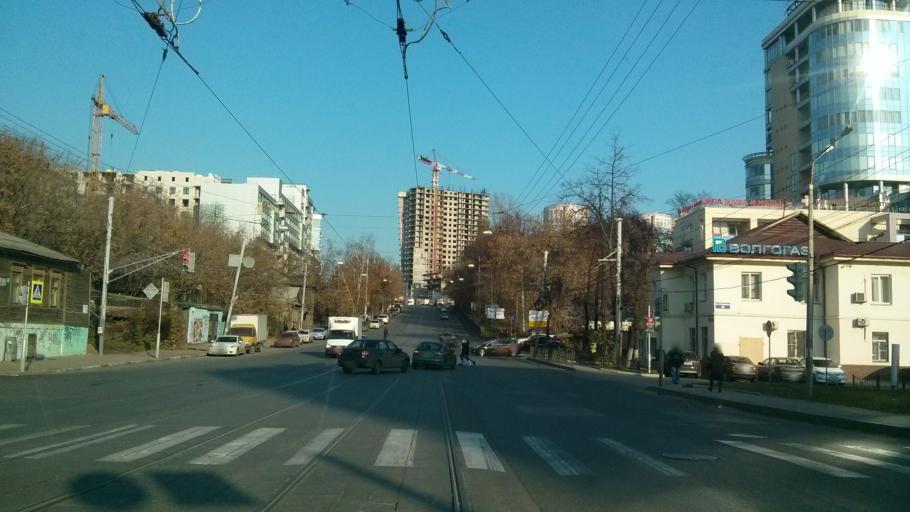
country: RU
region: Nizjnij Novgorod
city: Nizhniy Novgorod
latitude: 56.3203
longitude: 44.0305
